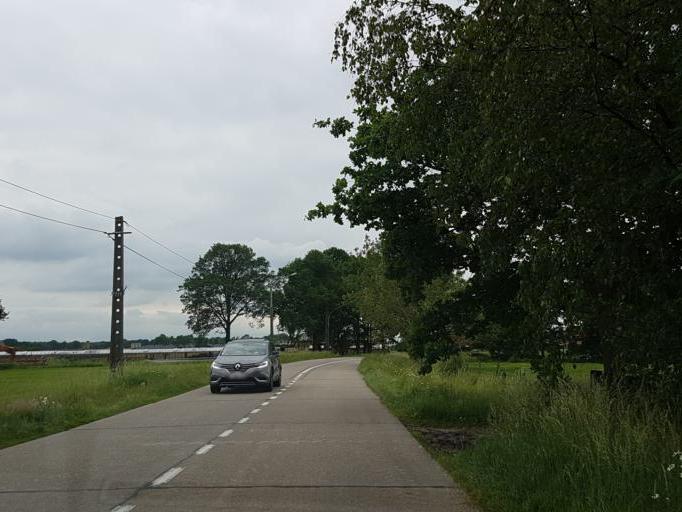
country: BE
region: Flanders
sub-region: Provincie Antwerpen
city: Rijkevorsel
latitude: 51.3679
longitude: 4.8004
